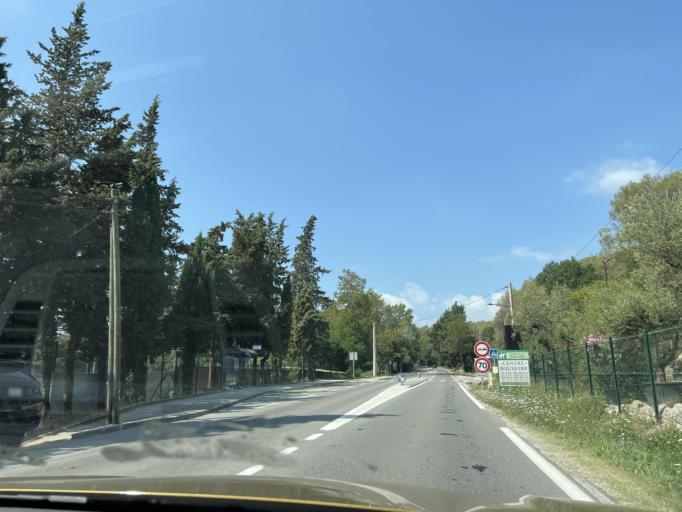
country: FR
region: Provence-Alpes-Cote d'Azur
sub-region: Departement des Alpes-Maritimes
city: Villeneuve-Loubet
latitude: 43.6590
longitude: 7.0942
